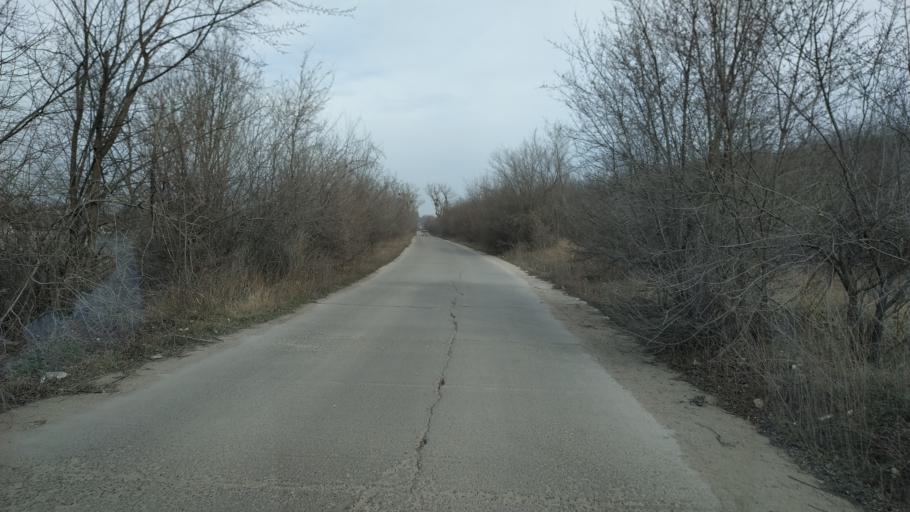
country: MD
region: Chisinau
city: Vatra
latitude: 47.0825
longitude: 28.7416
